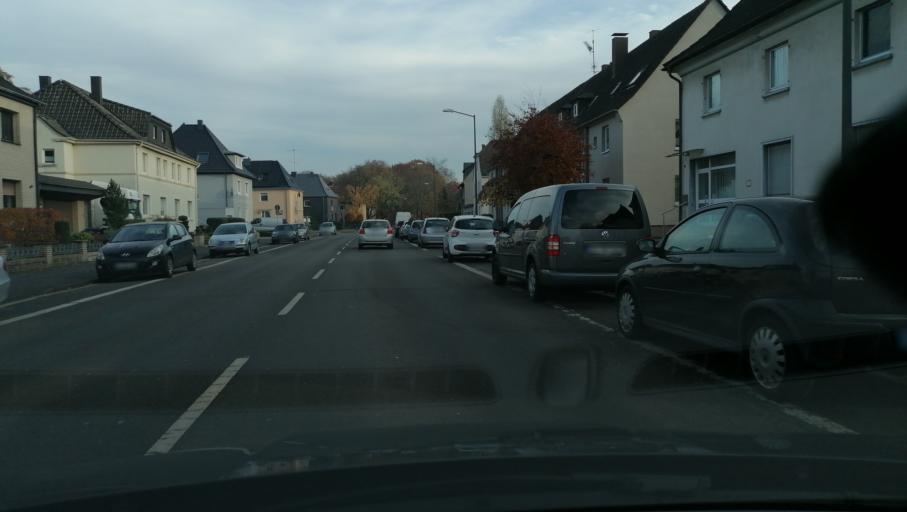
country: DE
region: North Rhine-Westphalia
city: Castrop-Rauxel
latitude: 51.5883
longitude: 7.3171
